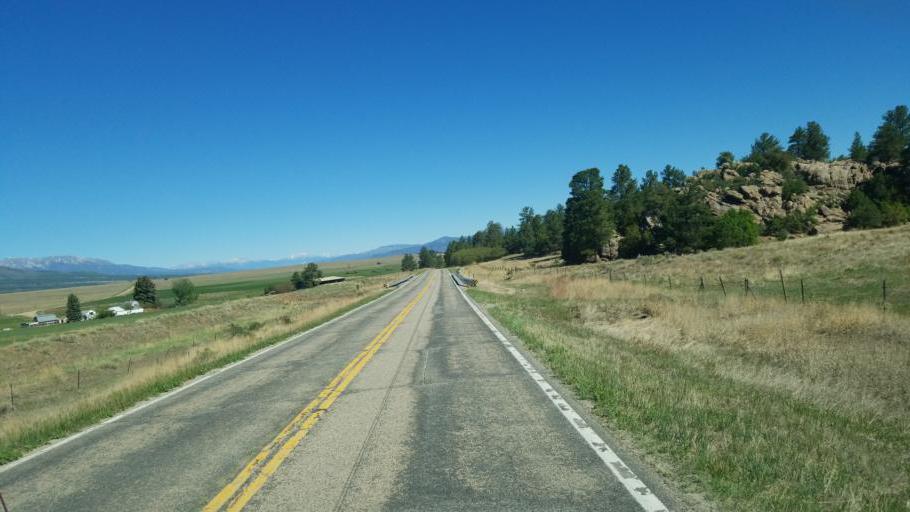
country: US
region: Colorado
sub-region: Custer County
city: Westcliffe
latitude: 38.2141
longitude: -105.5480
